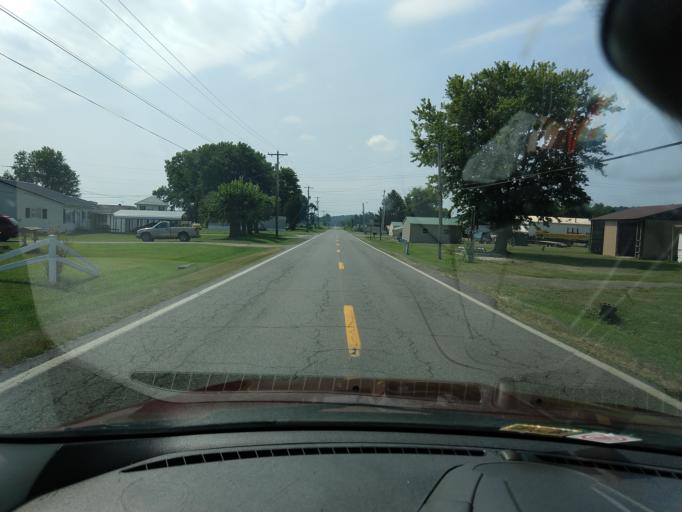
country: US
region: West Virginia
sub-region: Mason County
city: New Haven
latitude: 38.9530
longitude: -81.9220
